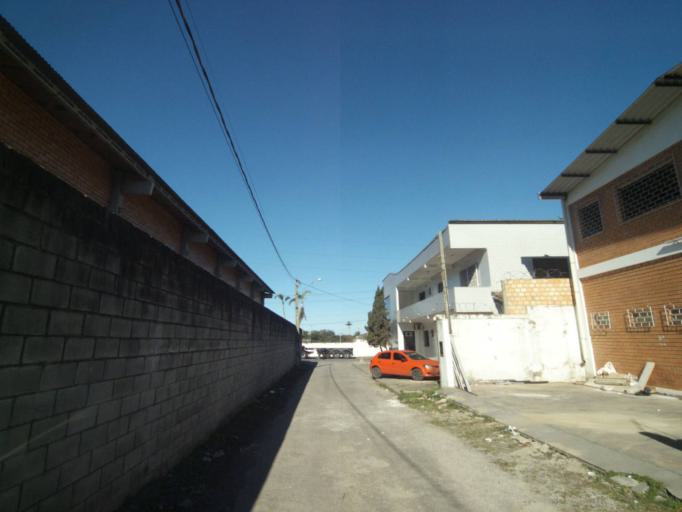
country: BR
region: Parana
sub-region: Paranagua
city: Paranagua
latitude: -25.5102
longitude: -48.5068
